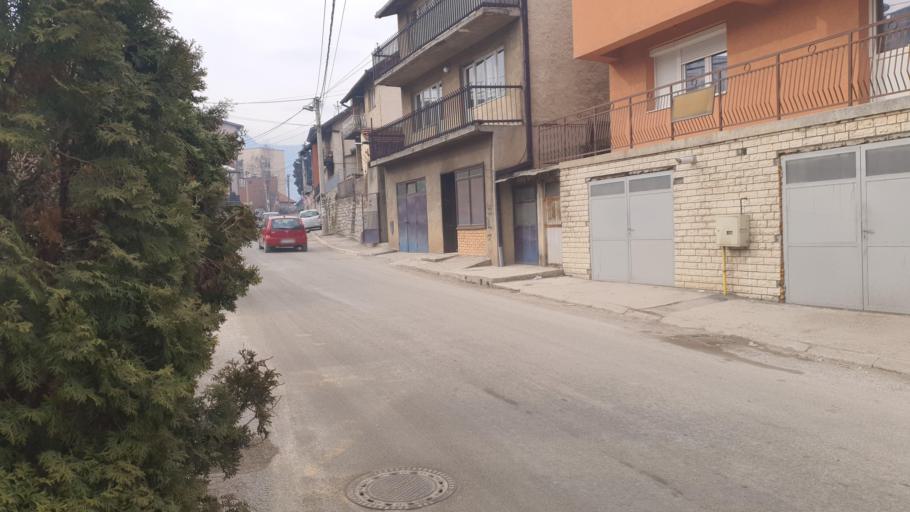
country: RS
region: Central Serbia
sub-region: Zlatiborski Okrug
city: Uzice
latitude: 43.8611
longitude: 19.8396
